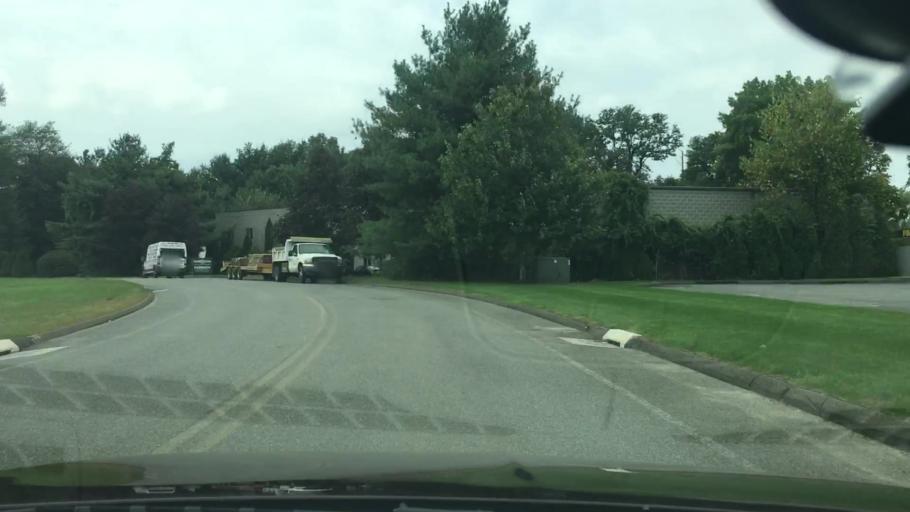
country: US
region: Connecticut
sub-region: Hartford County
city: South Windsor
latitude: 41.8600
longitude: -72.5971
